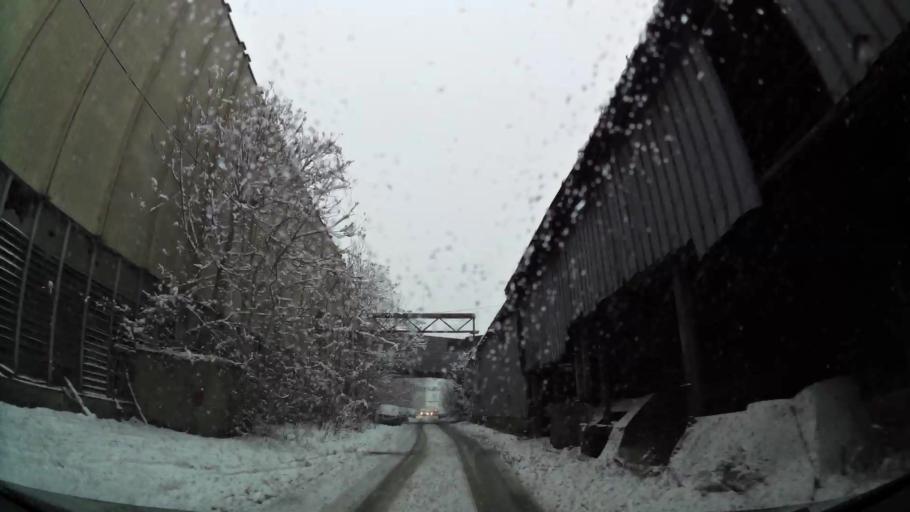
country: RS
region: Central Serbia
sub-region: Belgrade
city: Novi Beograd
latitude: 44.8096
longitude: 20.3954
